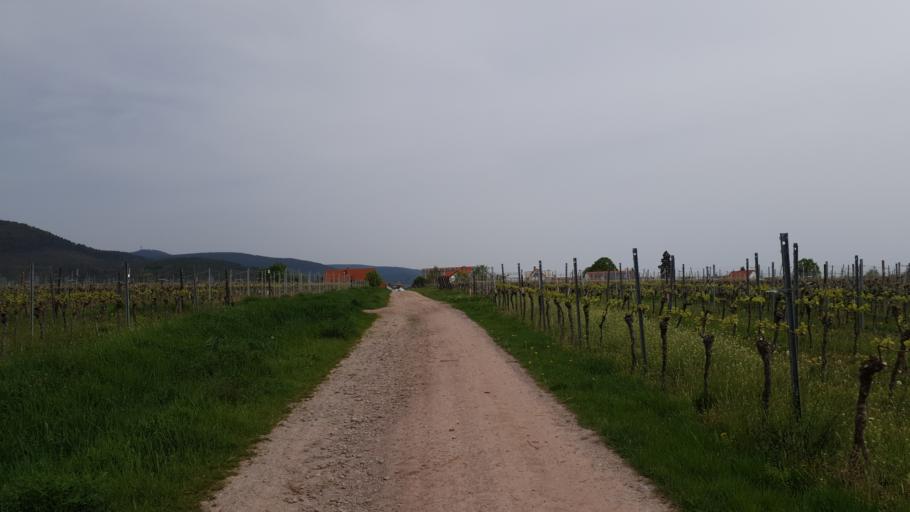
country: DE
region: Rheinland-Pfalz
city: Rhodt unter Rietburg
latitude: 49.2690
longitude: 8.0988
